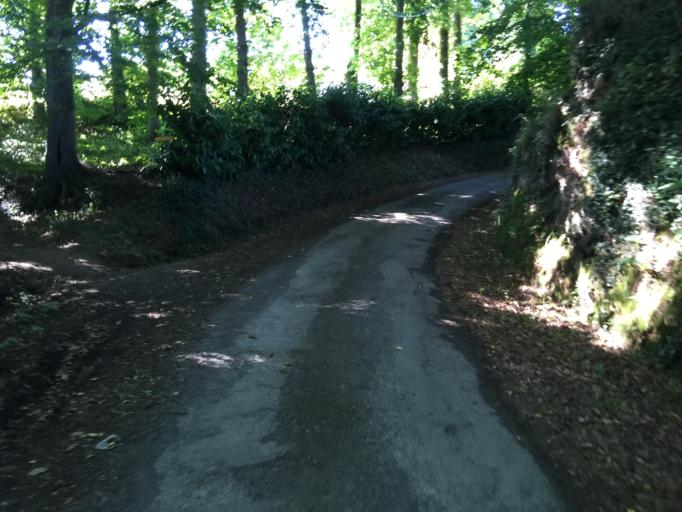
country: FR
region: Brittany
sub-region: Departement des Cotes-d'Armor
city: Pleslin-Trigavou
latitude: 48.5309
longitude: -2.0577
